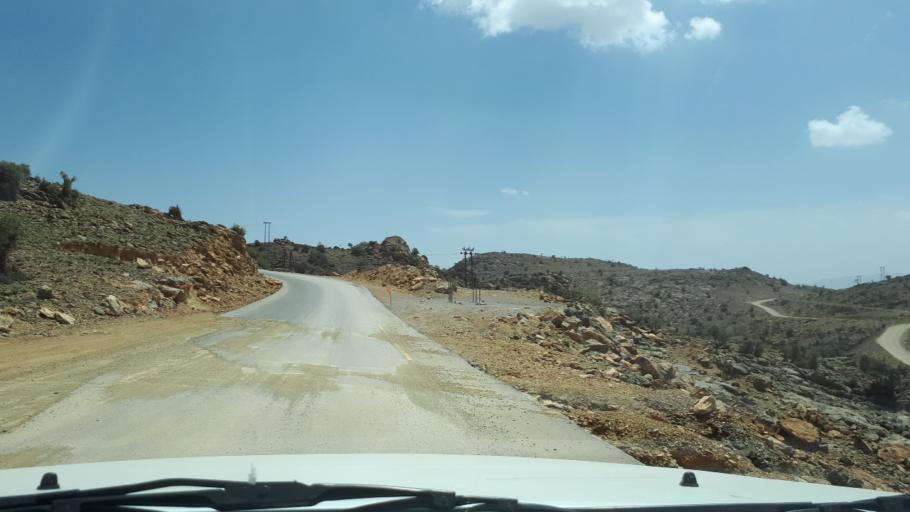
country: OM
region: Al Batinah
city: Rustaq
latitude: 23.2391
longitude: 57.1978
